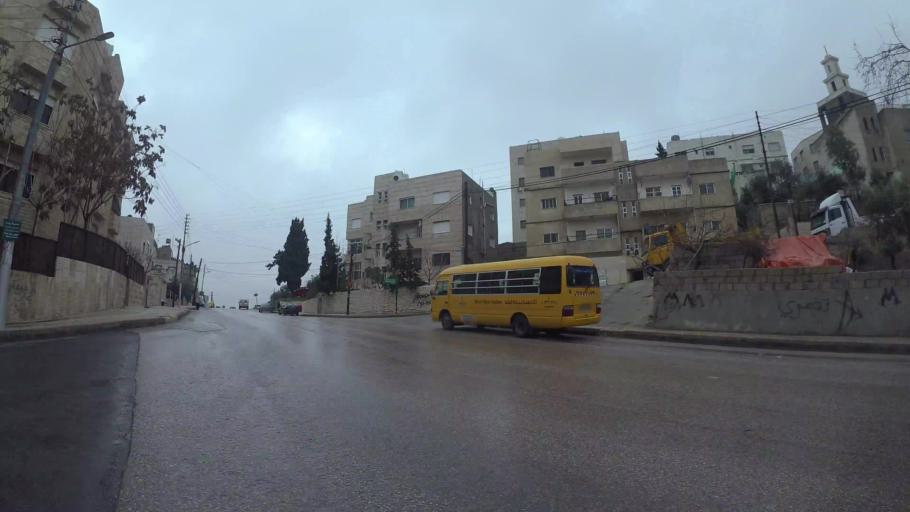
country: JO
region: Amman
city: Al Jubayhah
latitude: 32.0213
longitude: 35.8359
